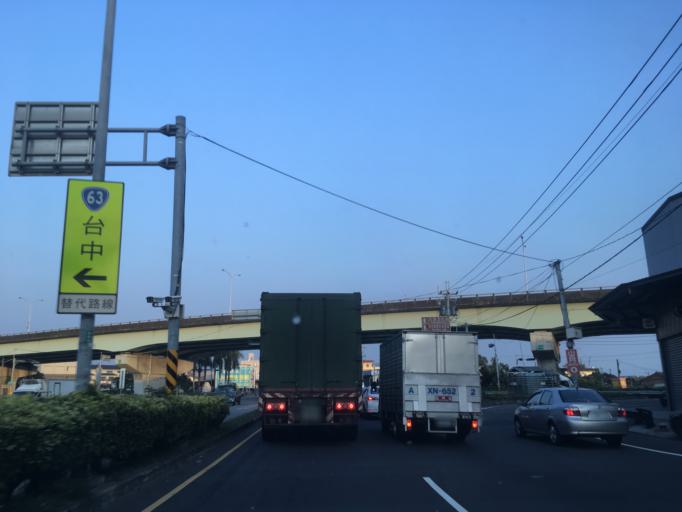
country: TW
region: Taiwan
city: Zhongxing New Village
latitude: 23.9985
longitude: 120.6609
